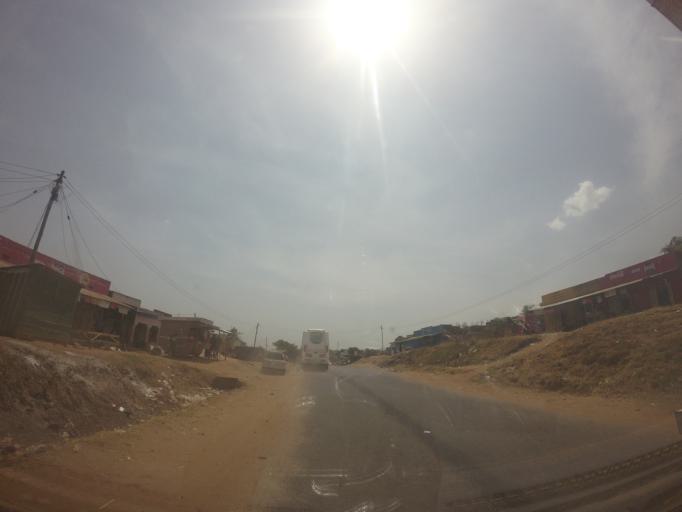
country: UG
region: Northern Region
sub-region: Arua District
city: Arua
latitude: 2.9508
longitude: 30.9323
